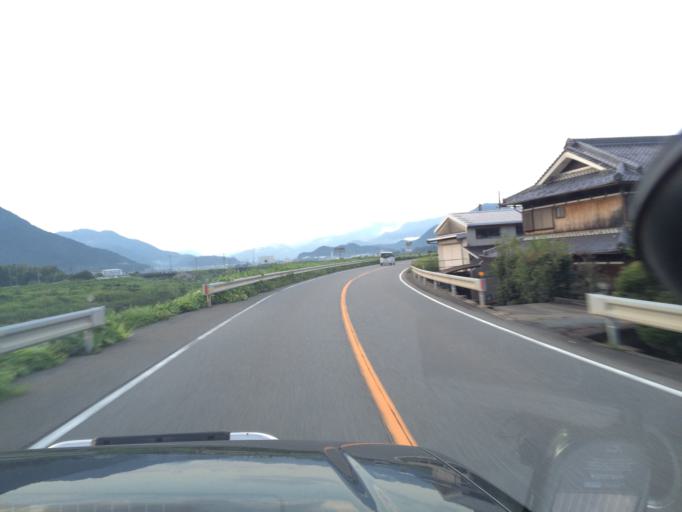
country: JP
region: Hyogo
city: Nishiwaki
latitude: 35.1413
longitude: 135.0284
